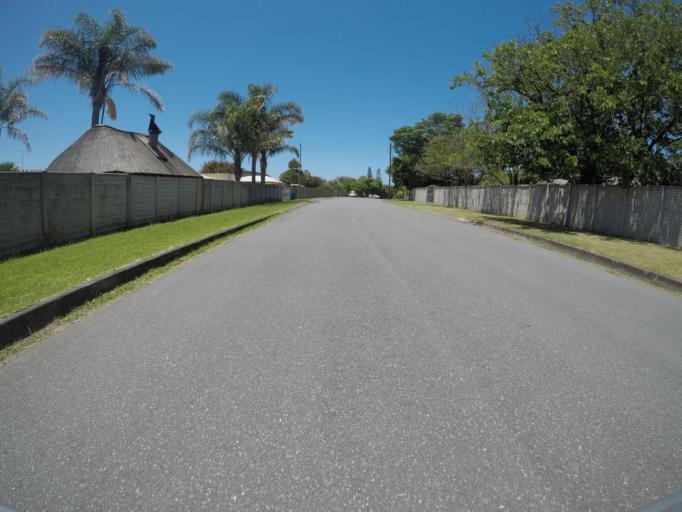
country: ZA
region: Eastern Cape
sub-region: Buffalo City Metropolitan Municipality
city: East London
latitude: -32.9654
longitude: 27.9433
